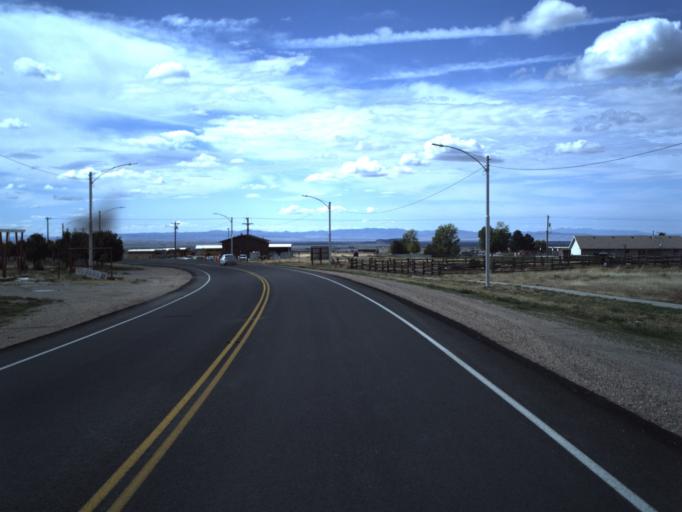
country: US
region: Utah
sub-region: Millard County
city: Fillmore
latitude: 38.9580
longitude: -112.3323
